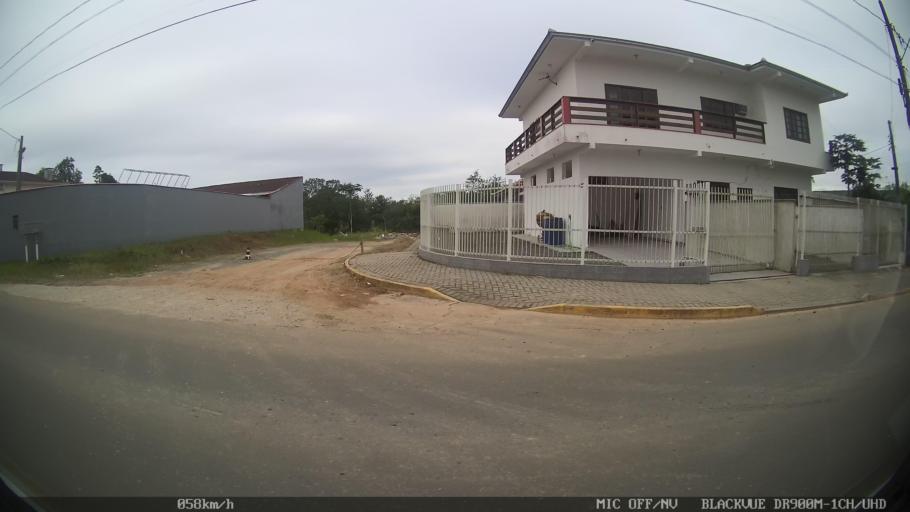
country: BR
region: Santa Catarina
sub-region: Joinville
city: Joinville
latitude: -26.3344
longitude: -48.9085
